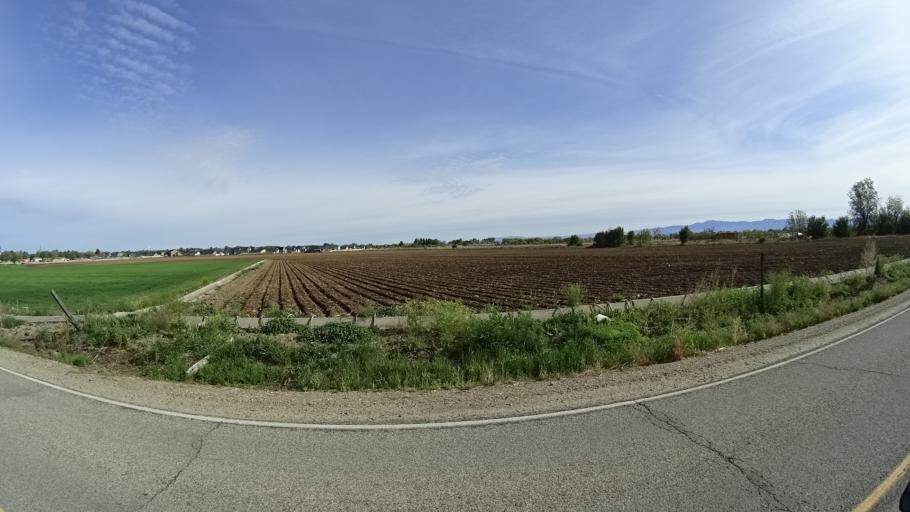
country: US
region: Idaho
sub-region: Ada County
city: Kuna
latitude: 43.4734
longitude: -116.3971
